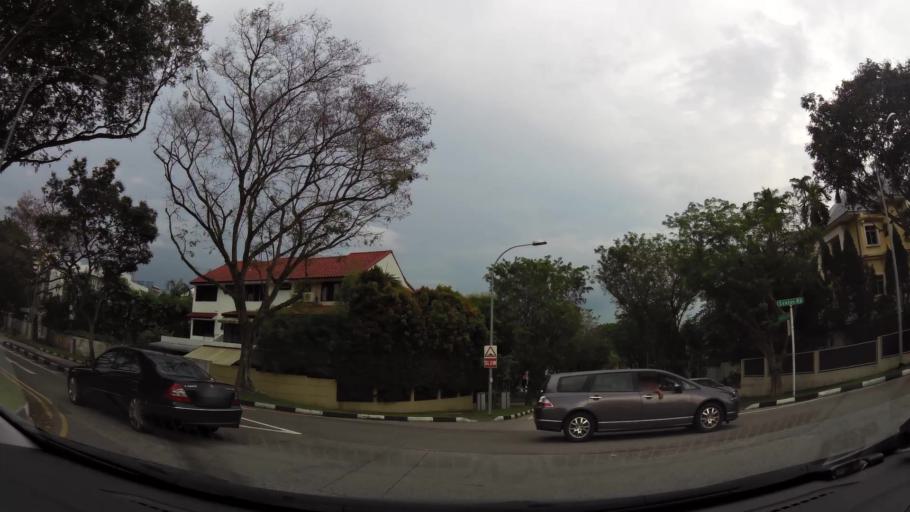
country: MY
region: Johor
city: Kampung Pasir Gudang Baru
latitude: 1.3881
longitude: 103.8379
